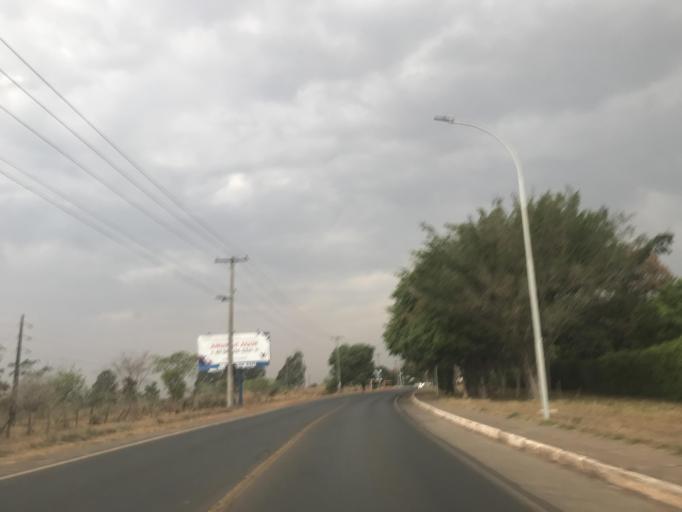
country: BR
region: Federal District
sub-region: Brasilia
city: Brasilia
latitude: -15.6670
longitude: -47.8184
